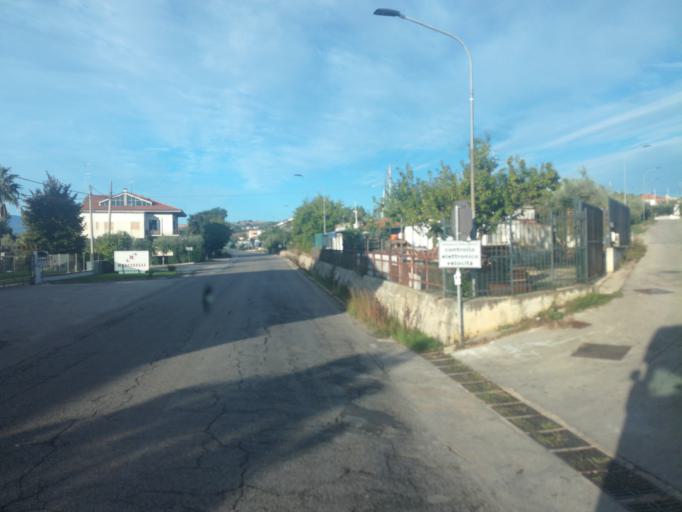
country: IT
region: Abruzzo
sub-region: Provincia di Chieti
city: Miglianico
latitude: 42.3686
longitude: 14.2890
